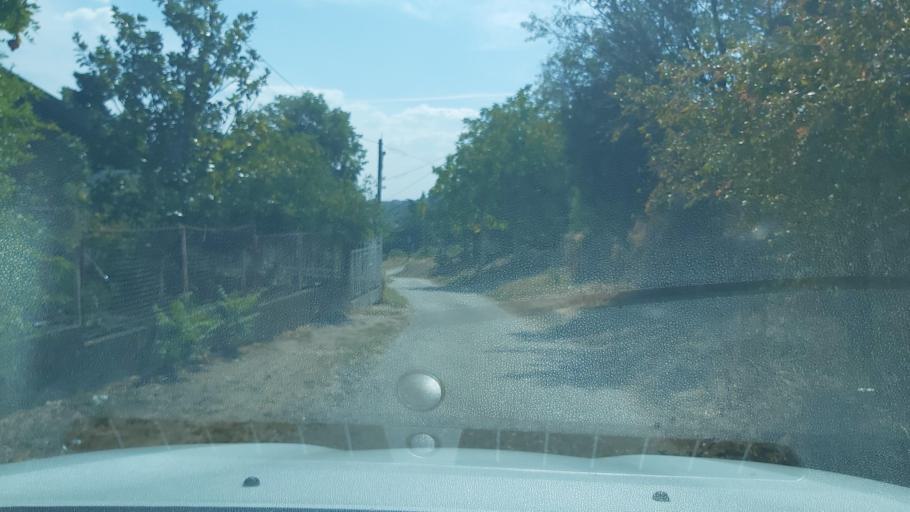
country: MK
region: Dojran
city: Star Dojran
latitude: 41.1806
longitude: 22.7228
